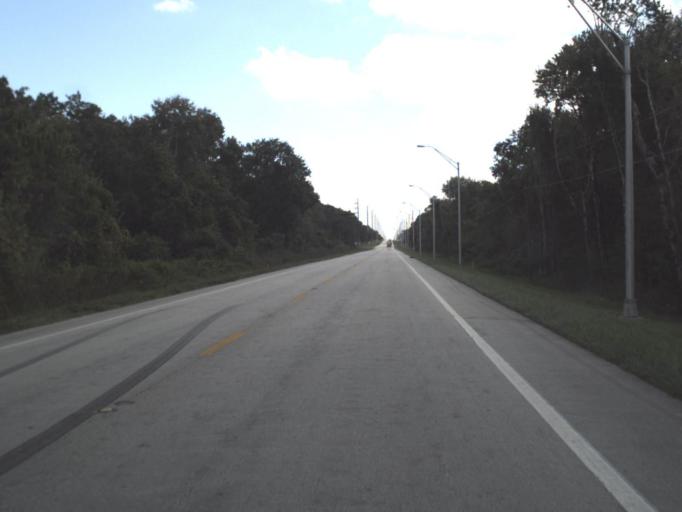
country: US
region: Florida
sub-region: Highlands County
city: Sebring
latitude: 27.4123
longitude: -81.5207
